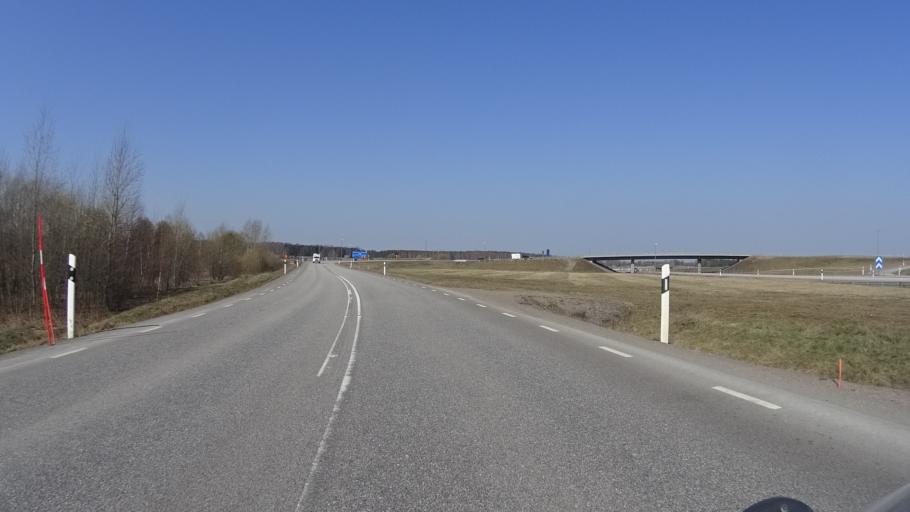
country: SE
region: OEstergoetland
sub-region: Mjolby Kommun
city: Mjolby
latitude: 58.4016
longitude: 15.0946
